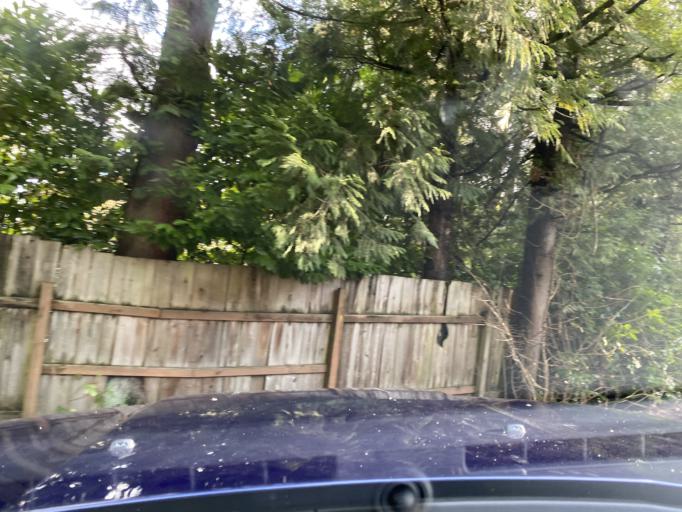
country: US
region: Washington
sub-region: King County
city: West Lake Sammamish
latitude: 47.5641
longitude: -122.0955
